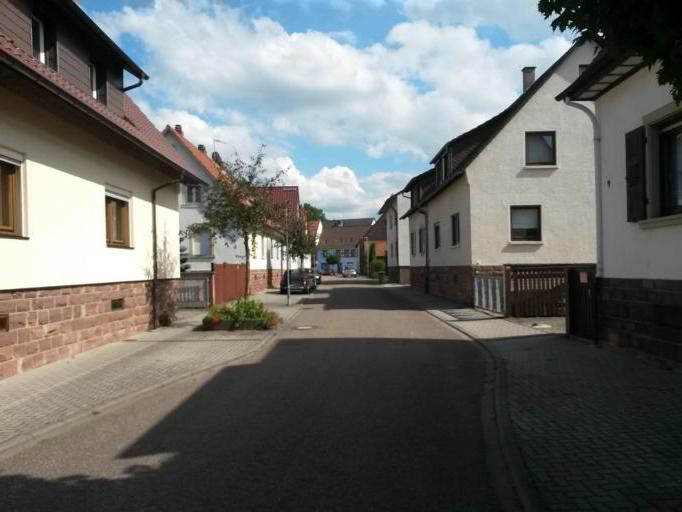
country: DE
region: Baden-Wuerttemberg
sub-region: Karlsruhe Region
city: Konigsbach-Stein
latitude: 48.9456
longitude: 8.5721
